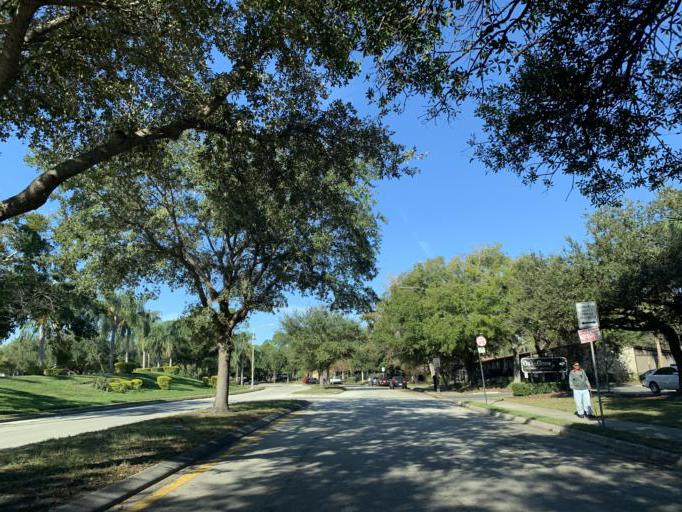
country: US
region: Florida
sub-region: Orange County
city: Oak Ridge
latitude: 28.4905
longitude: -81.4396
